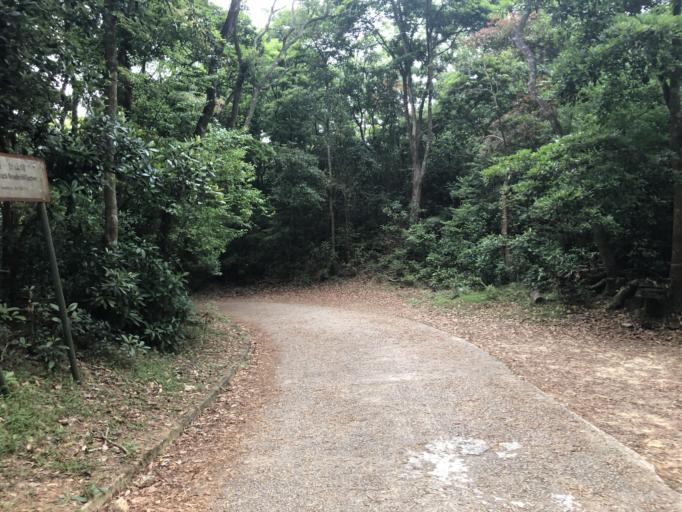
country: HK
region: Sha Tin
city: Sha Tin
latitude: 22.3948
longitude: 114.1681
